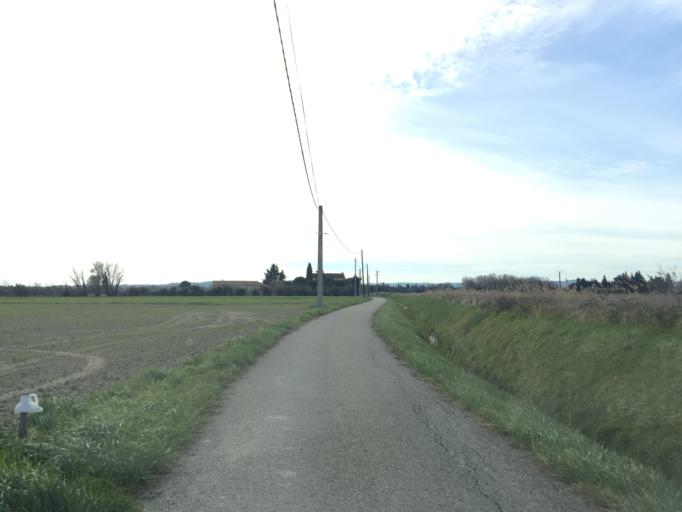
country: FR
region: Provence-Alpes-Cote d'Azur
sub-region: Departement du Vaucluse
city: Caderousse
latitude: 44.1227
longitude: 4.7482
